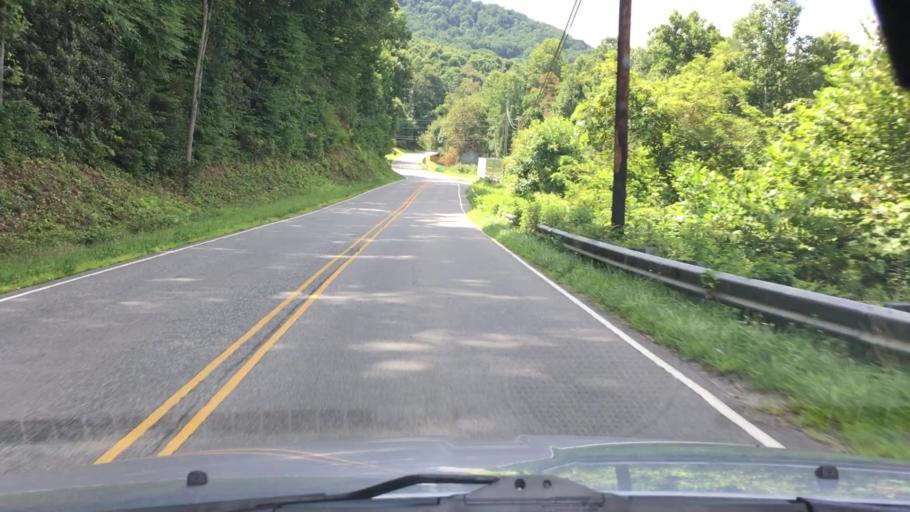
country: US
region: North Carolina
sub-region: Yancey County
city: Burnsville
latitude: 35.8685
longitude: -82.2044
